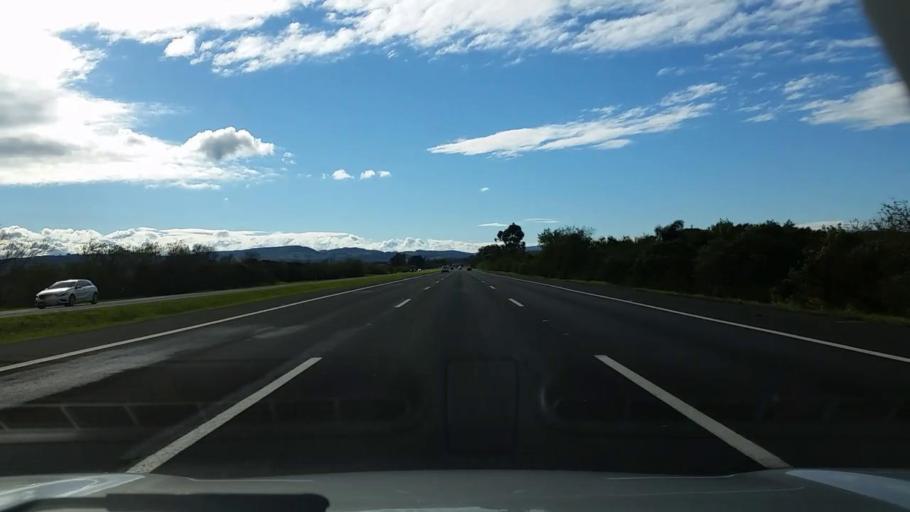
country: BR
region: Rio Grande do Sul
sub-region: Rolante
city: Rolante
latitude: -29.8821
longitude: -50.5283
